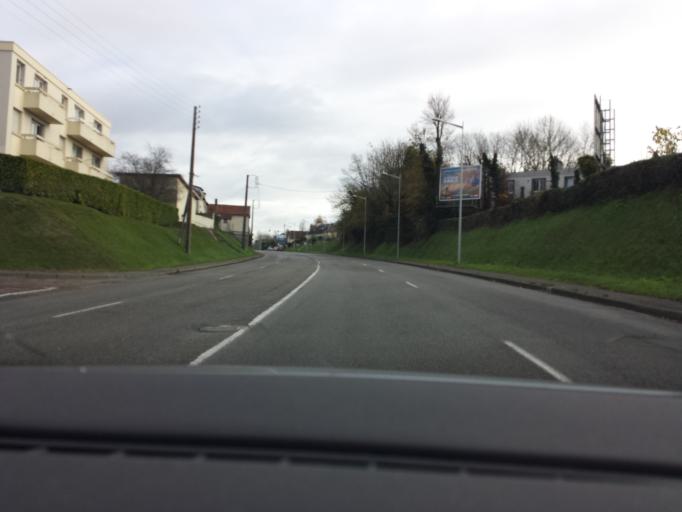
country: FR
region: Haute-Normandie
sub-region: Departement de l'Eure
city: Evreux
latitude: 49.0162
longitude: 1.1623
